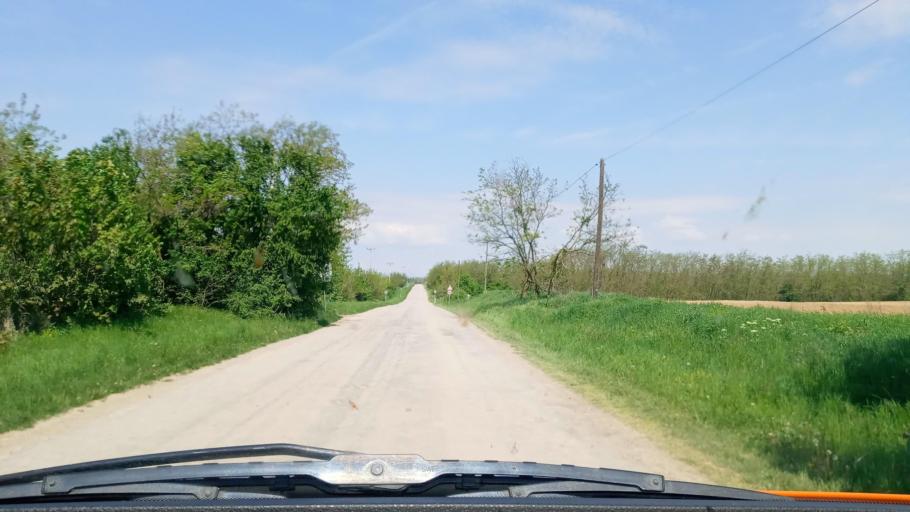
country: HU
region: Baranya
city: Boly
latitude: 45.8953
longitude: 18.5587
